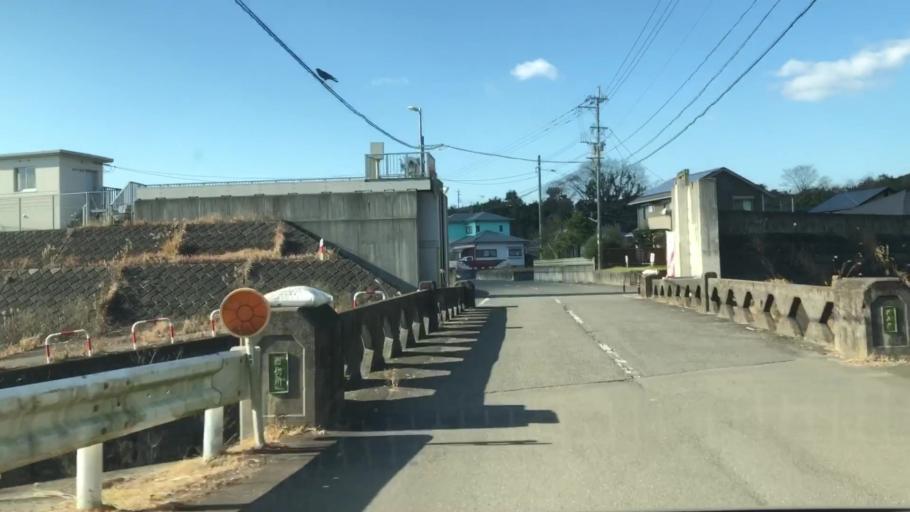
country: JP
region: Kagoshima
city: Satsumasendai
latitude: 31.8593
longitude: 130.3527
